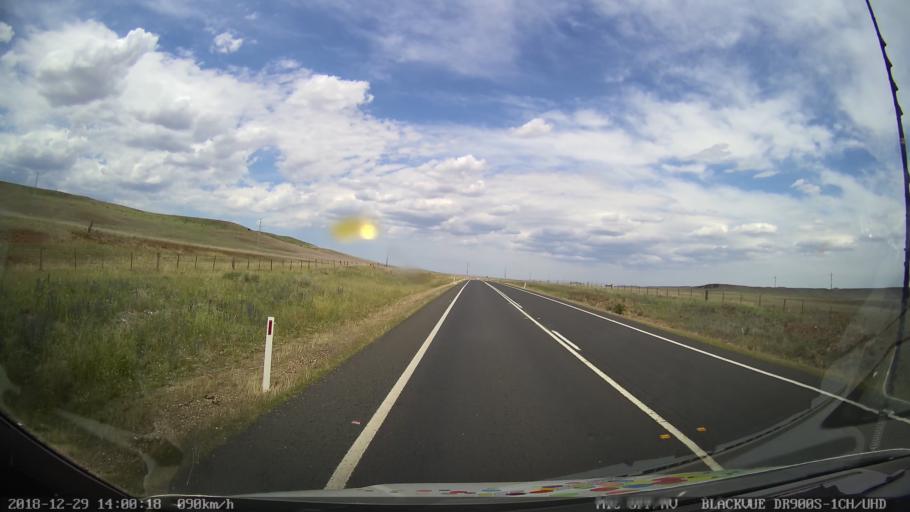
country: AU
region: New South Wales
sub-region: Cooma-Monaro
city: Cooma
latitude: -36.2627
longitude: 149.1569
